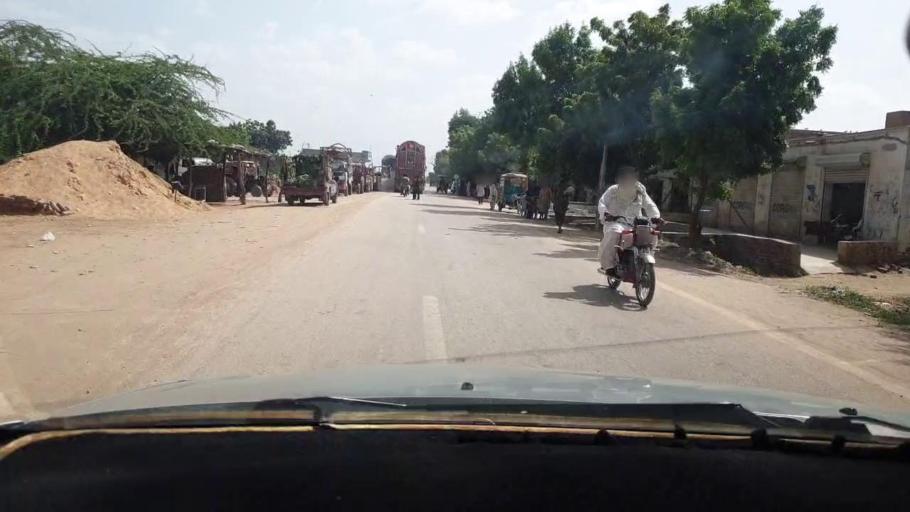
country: PK
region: Sindh
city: Digri
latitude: 25.0675
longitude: 69.2178
